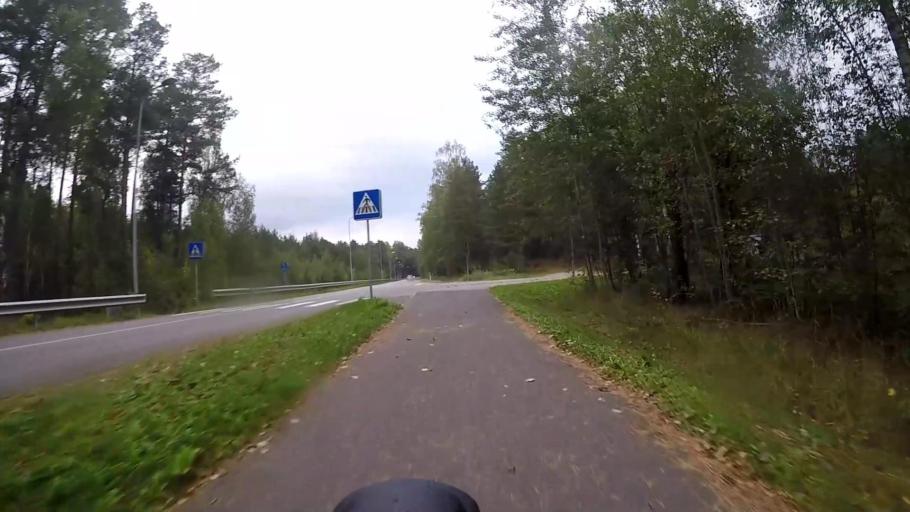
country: LV
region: Saulkrastu
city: Saulkrasti
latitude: 57.2662
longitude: 24.4278
